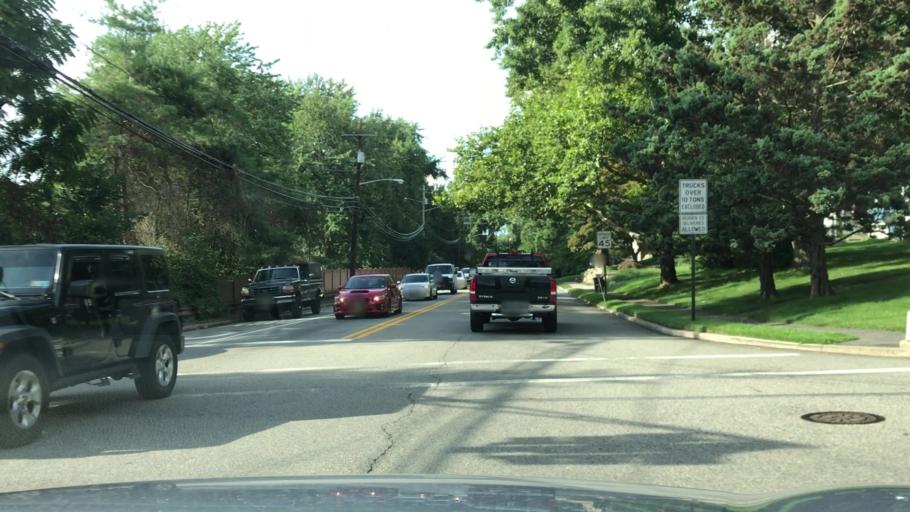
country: US
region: New Jersey
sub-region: Bergen County
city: Haworth
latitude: 40.9686
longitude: -73.9830
